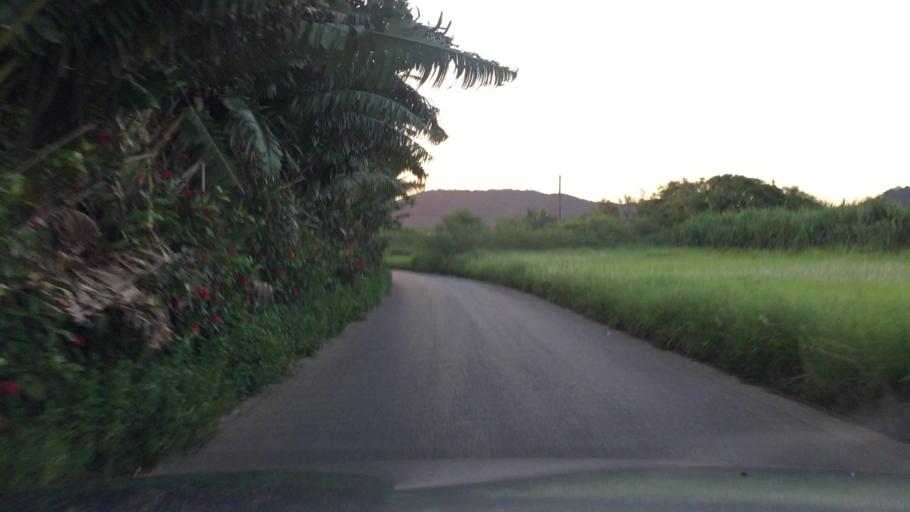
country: JP
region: Okinawa
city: Ishigaki
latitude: 24.3541
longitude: 124.1627
